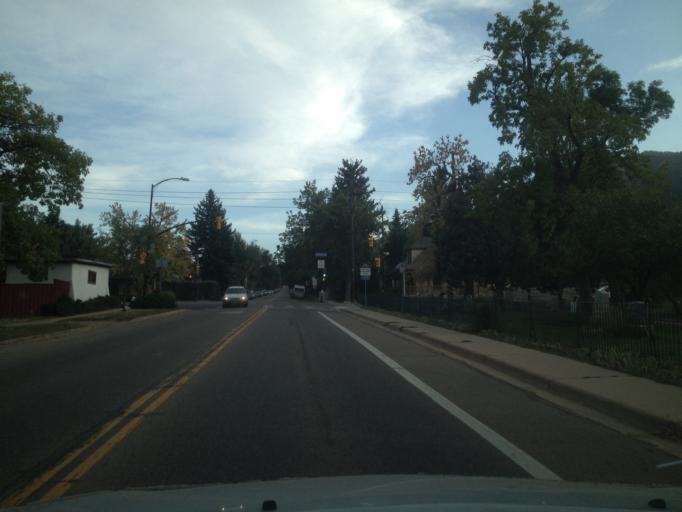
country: US
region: Colorado
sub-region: Boulder County
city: Boulder
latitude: 40.0078
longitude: -105.2820
